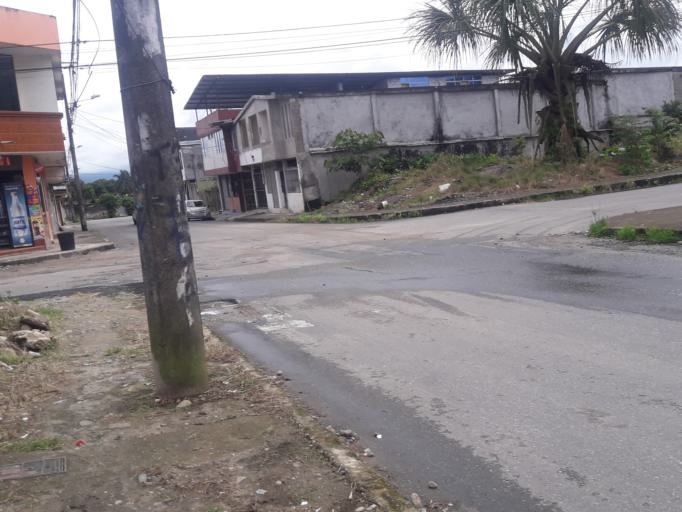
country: EC
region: Napo
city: Tena
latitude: -0.9978
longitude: -77.8093
